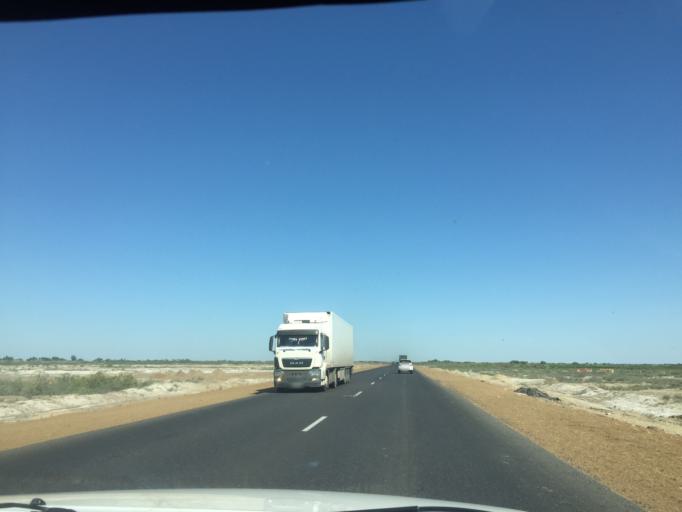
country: KZ
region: Qyzylorda
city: Dzhalagash
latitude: 44.8753
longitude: 64.7983
